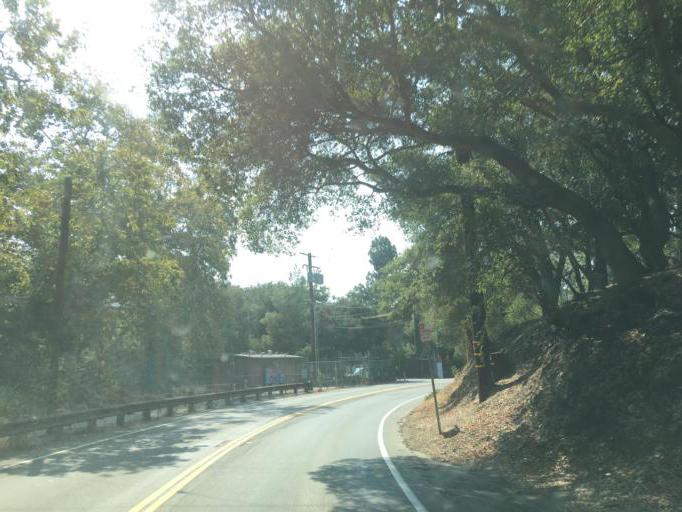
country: US
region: California
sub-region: Los Angeles County
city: Topanga
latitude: 34.0910
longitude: -118.6055
